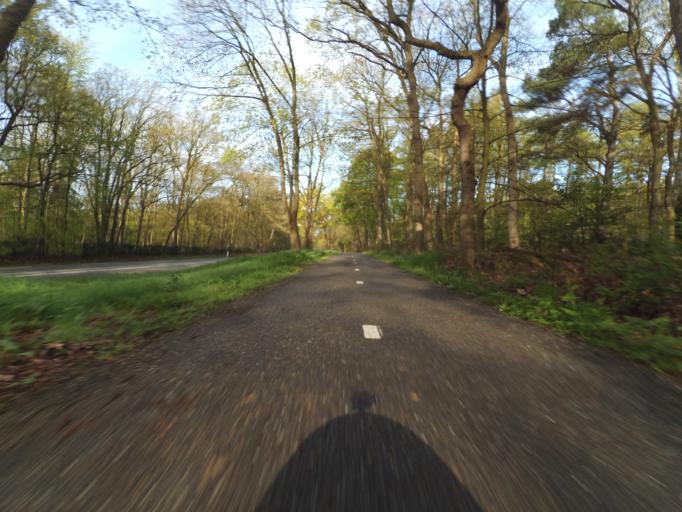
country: NL
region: Utrecht
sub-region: Gemeente Utrechtse Heuvelrug
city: Doorn
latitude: 52.0344
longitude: 5.3596
